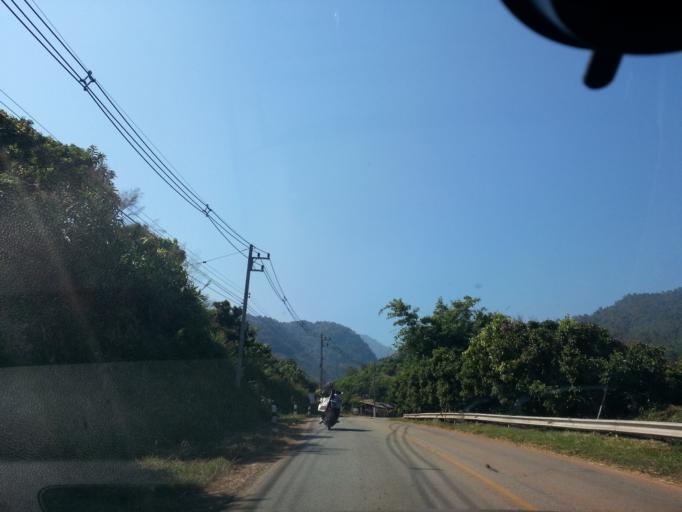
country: TH
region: Chiang Mai
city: Chai Prakan
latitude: 19.8291
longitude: 99.1032
